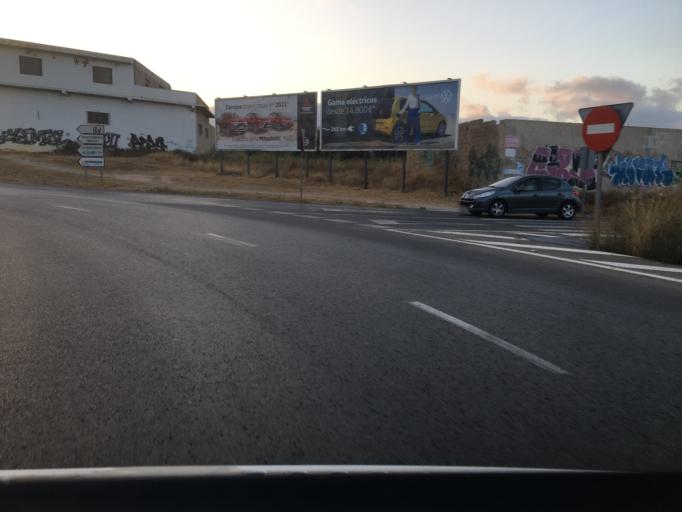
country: ES
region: Murcia
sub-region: Murcia
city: Cartagena
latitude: 37.6307
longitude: -0.9820
